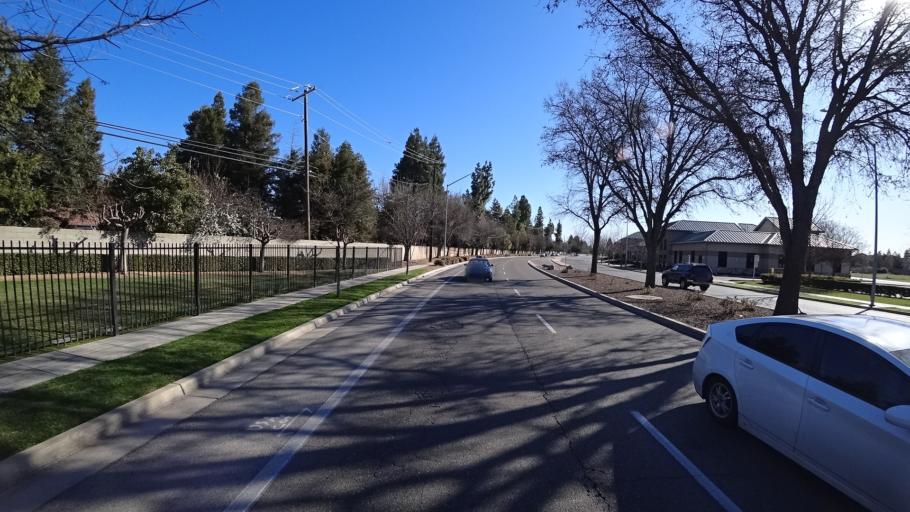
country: US
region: California
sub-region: Fresno County
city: West Park
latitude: 36.8298
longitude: -119.8662
